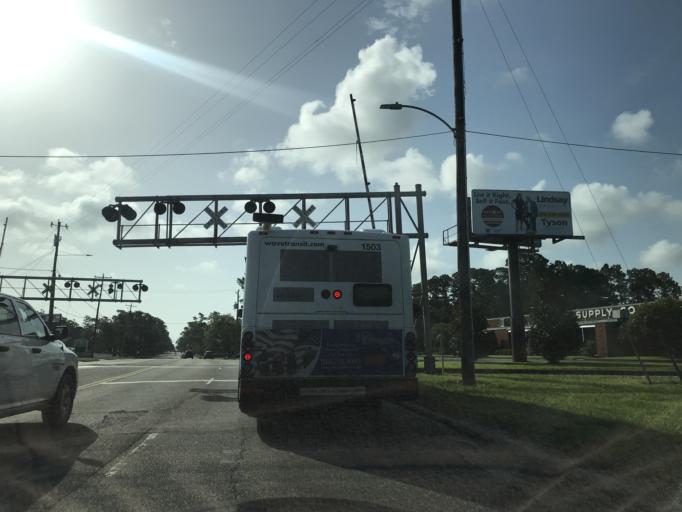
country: US
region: North Carolina
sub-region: New Hanover County
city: Wilmington
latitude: 34.2247
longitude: -77.9228
